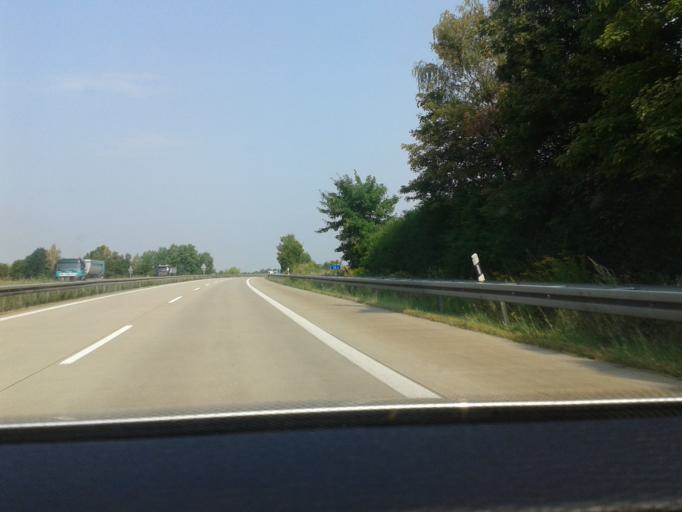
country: DE
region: Saxony
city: Mochau
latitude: 51.1372
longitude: 13.1548
